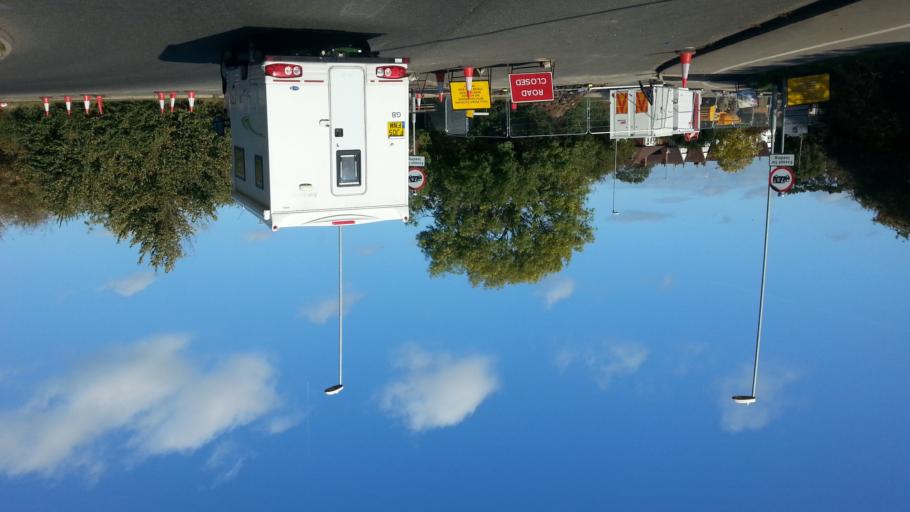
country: GB
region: England
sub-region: Northamptonshire
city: Thrapston
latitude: 52.3943
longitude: -0.5234
